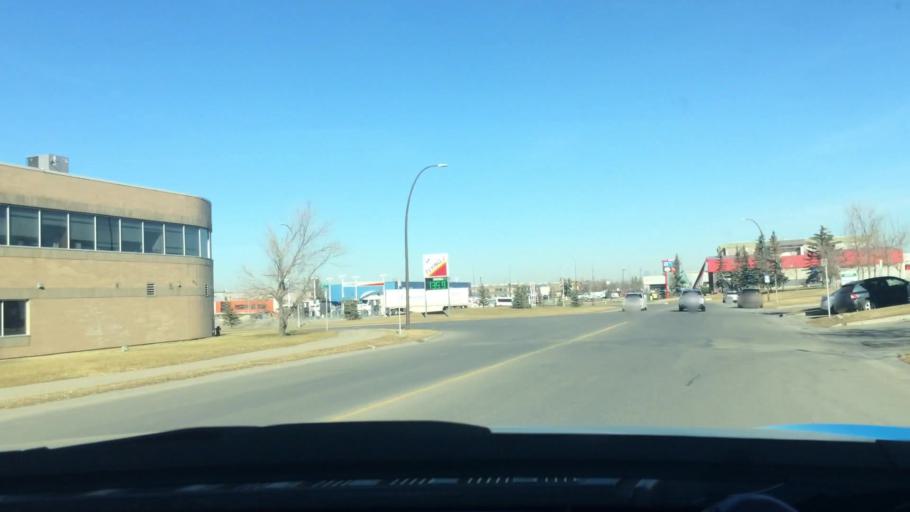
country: CA
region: Alberta
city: Calgary
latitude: 51.0737
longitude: -114.0041
